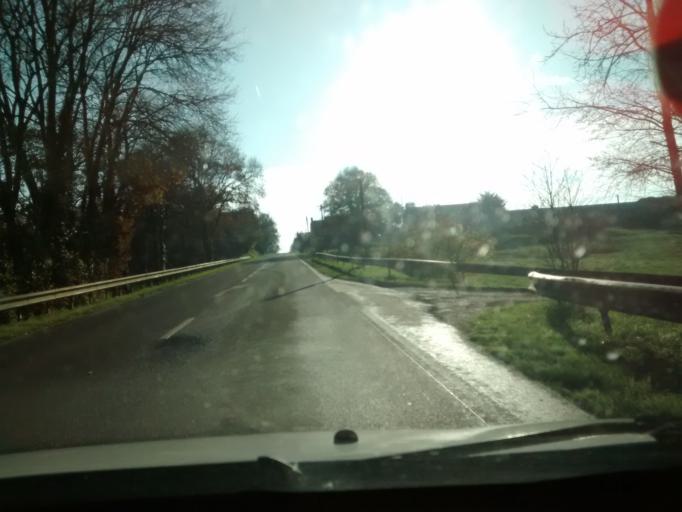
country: FR
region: Brittany
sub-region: Departement d'Ille-et-Vilaine
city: Sens-de-Bretagne
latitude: 48.3407
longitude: -1.5213
